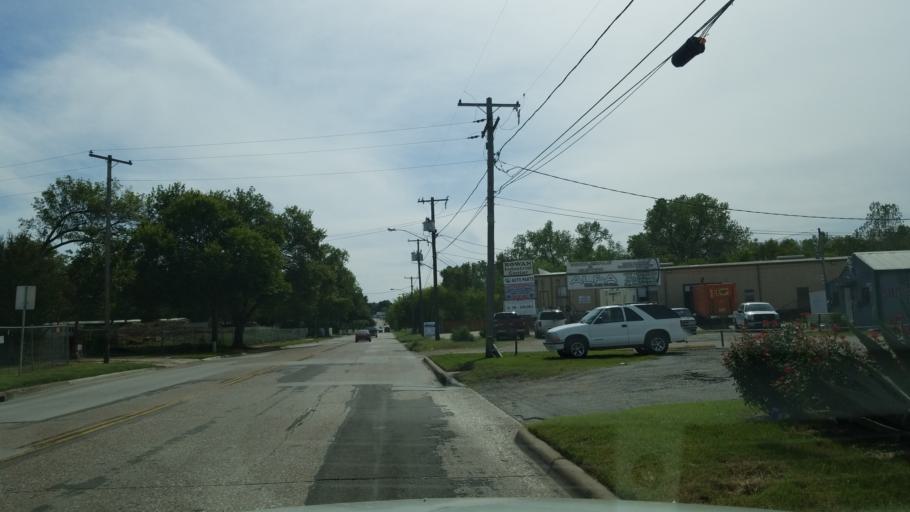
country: US
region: Texas
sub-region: Dallas County
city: Highland Park
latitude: 32.7903
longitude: -96.7253
